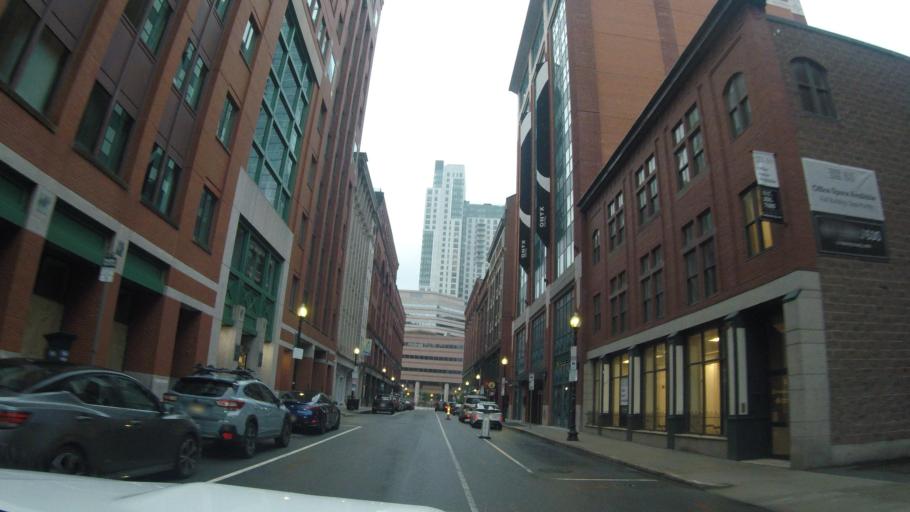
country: US
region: Massachusetts
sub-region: Suffolk County
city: Boston
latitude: 42.3642
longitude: -71.0607
